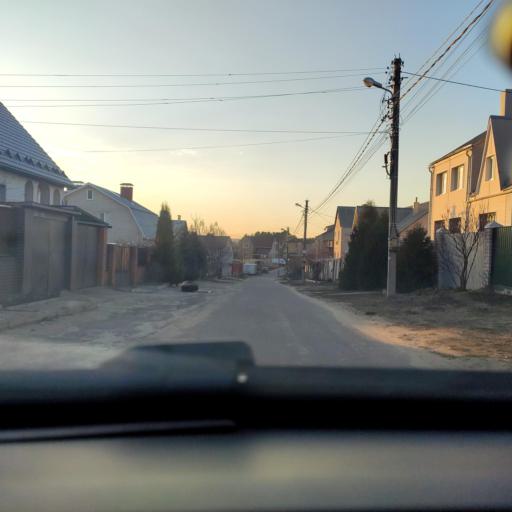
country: RU
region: Voronezj
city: Shilovo
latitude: 51.5759
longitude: 39.0469
